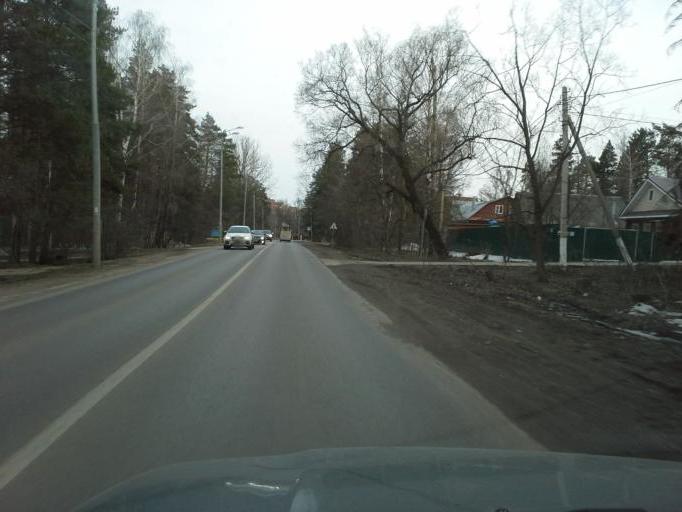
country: RU
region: Moskovskaya
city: Lesnoy Gorodok
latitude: 55.6447
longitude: 37.2057
